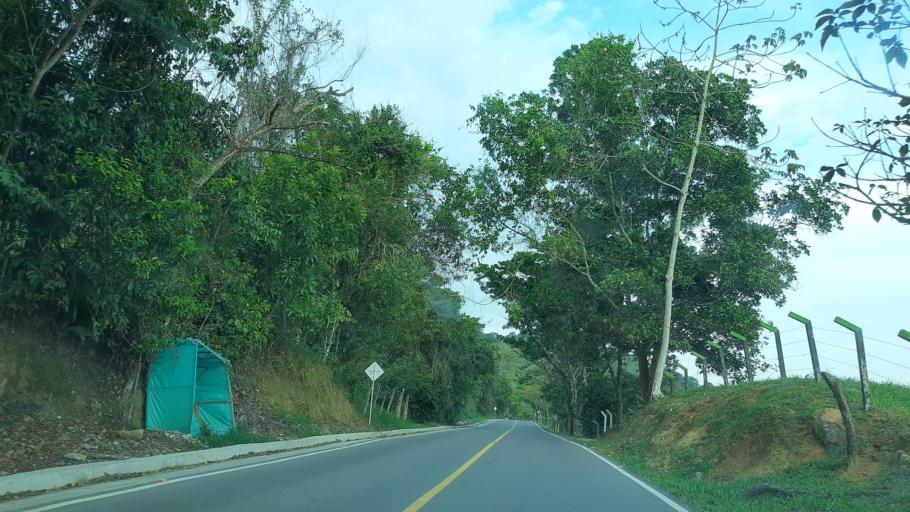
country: CO
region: Boyaca
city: San Luis de Gaceno
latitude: 4.8228
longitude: -73.1981
